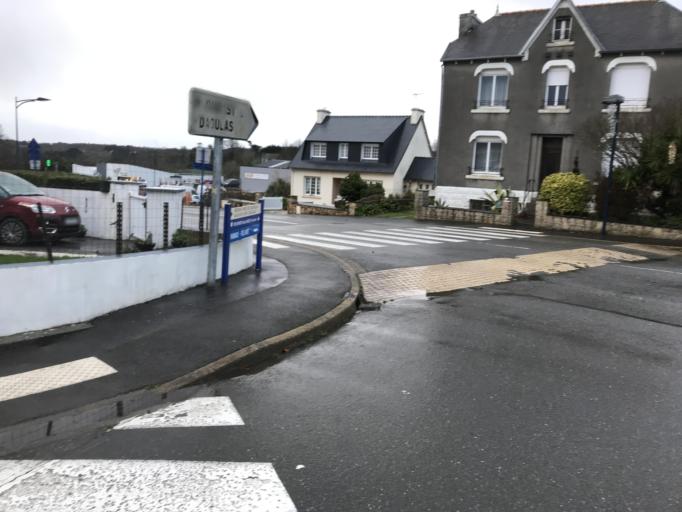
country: FR
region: Brittany
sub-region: Departement du Finistere
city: Loperhet
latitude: 48.3777
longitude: -4.3115
